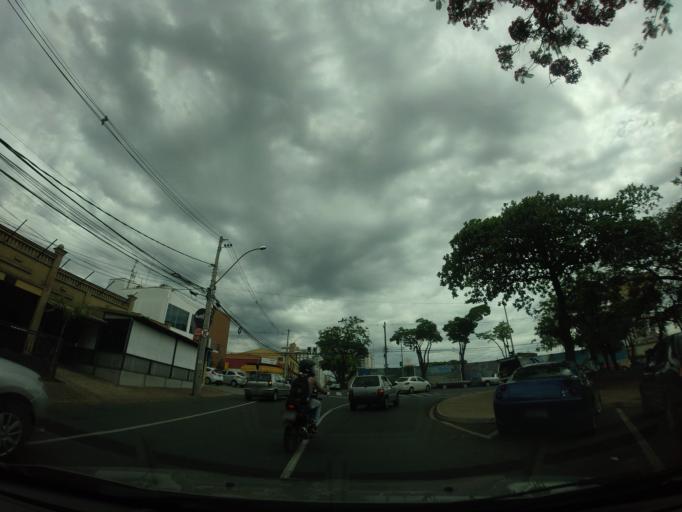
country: BR
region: Sao Paulo
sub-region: Piracicaba
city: Piracicaba
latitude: -22.7323
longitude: -47.6360
